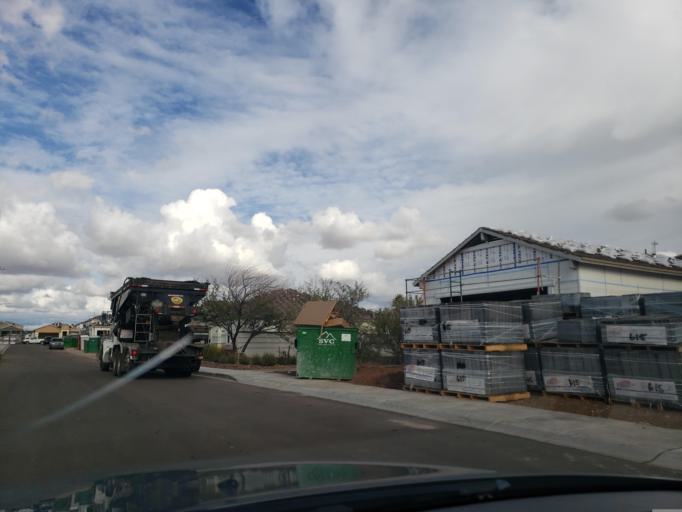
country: US
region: Arizona
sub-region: Maricopa County
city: Paradise Valley
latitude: 33.6445
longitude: -111.9694
